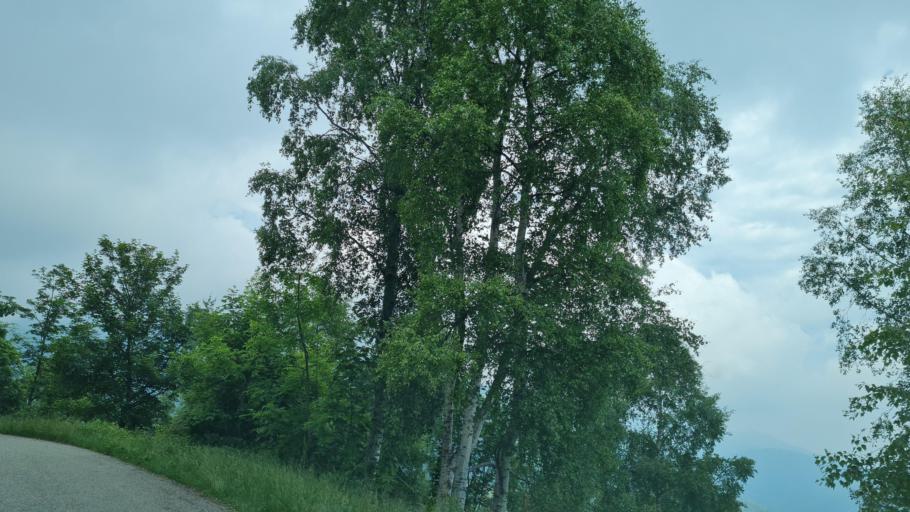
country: IT
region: Piedmont
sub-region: Provincia di Biella
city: Pollone
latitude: 45.6041
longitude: 7.9856
